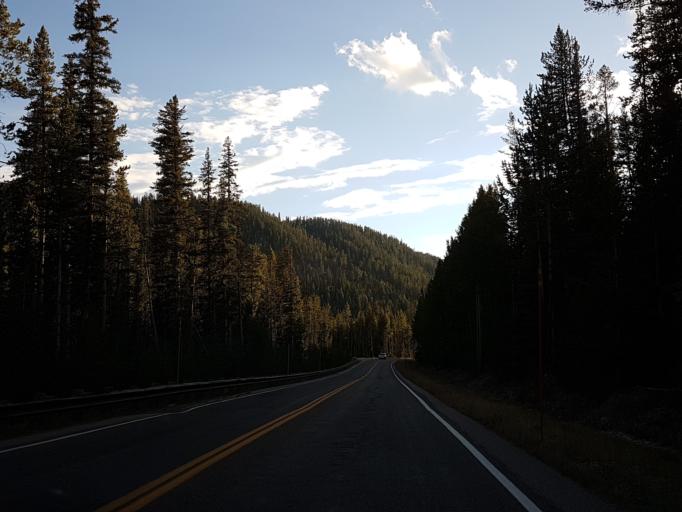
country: US
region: Montana
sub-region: Gallatin County
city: West Yellowstone
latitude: 44.4364
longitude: -110.7332
